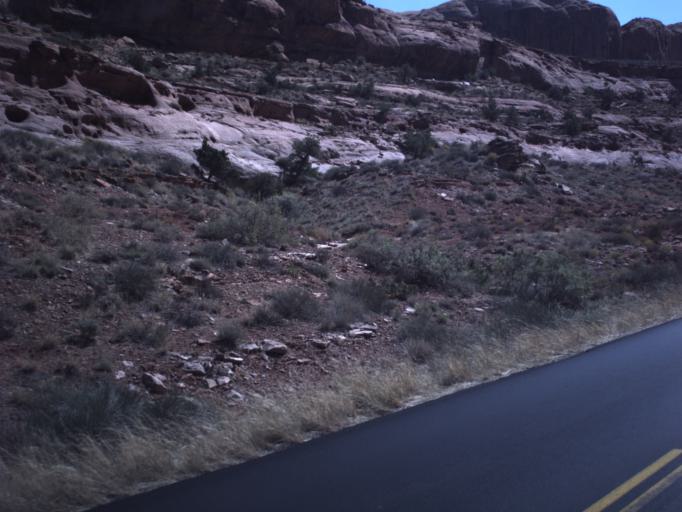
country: US
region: Utah
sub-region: Grand County
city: Moab
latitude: 38.6085
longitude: -109.5575
